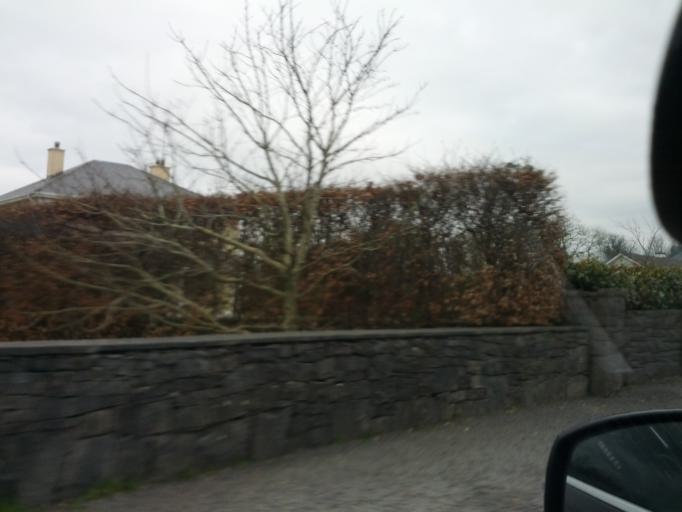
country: IE
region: Connaught
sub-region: County Galway
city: Athenry
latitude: 53.2611
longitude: -8.7402
